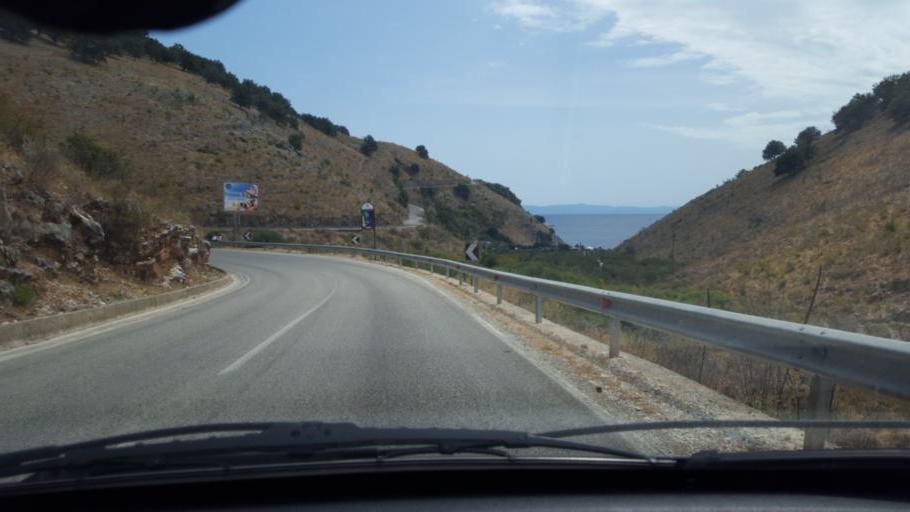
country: AL
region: Vlore
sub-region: Rrethi i Vlores
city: Himare
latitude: 40.0860
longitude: 19.7669
